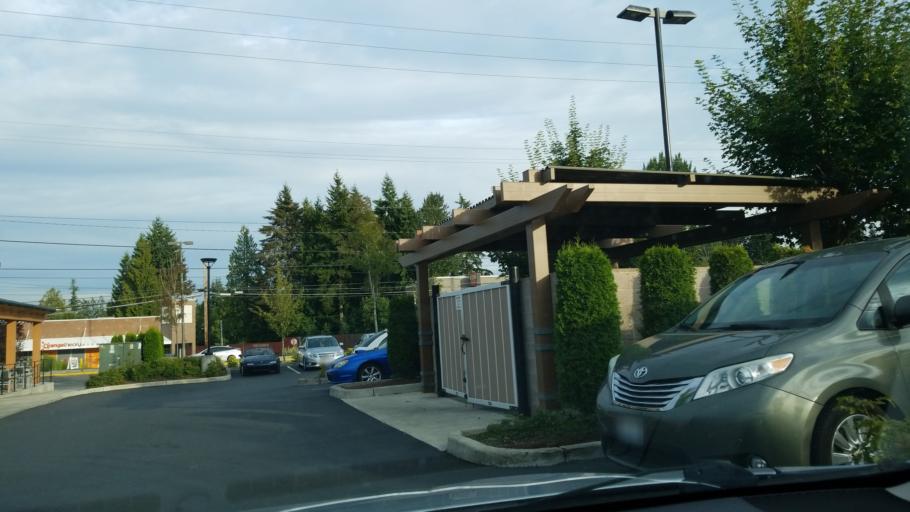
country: US
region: Washington
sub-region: Snohomish County
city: Lynnwood
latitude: 47.8197
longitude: -122.3173
